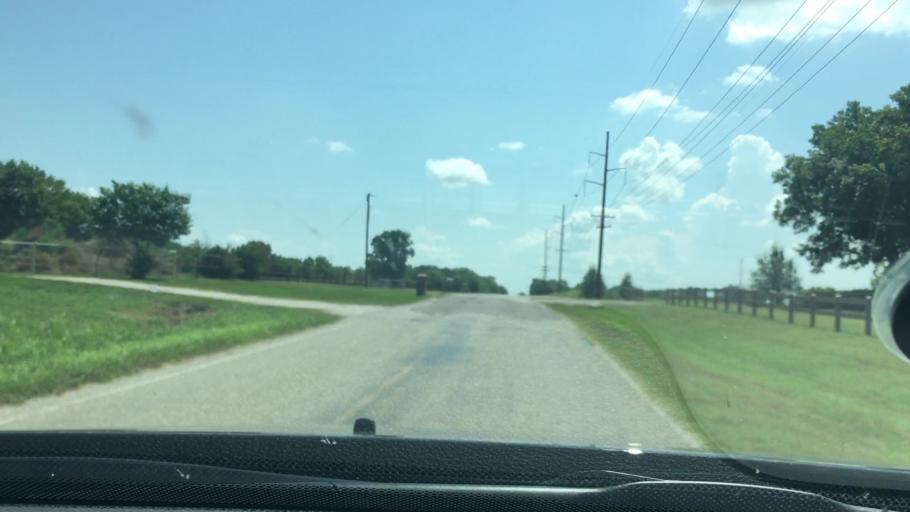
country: US
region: Oklahoma
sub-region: Pontotoc County
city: Ada
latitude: 34.6945
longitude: -96.5749
